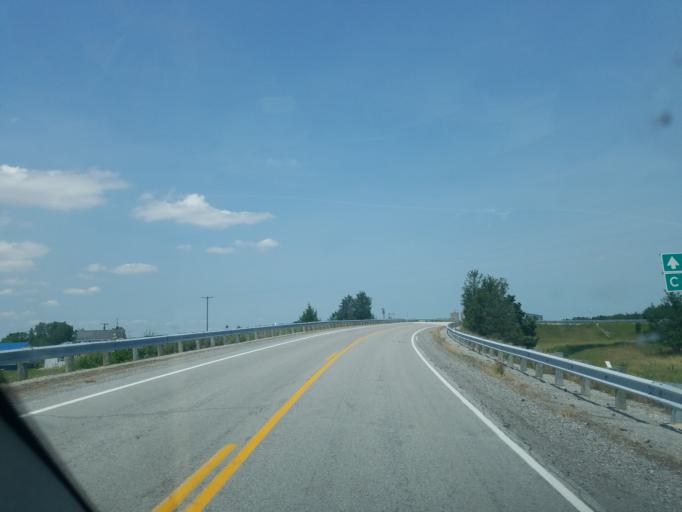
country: US
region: Ohio
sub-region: Wyandot County
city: Carey
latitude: 40.9677
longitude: -83.4857
